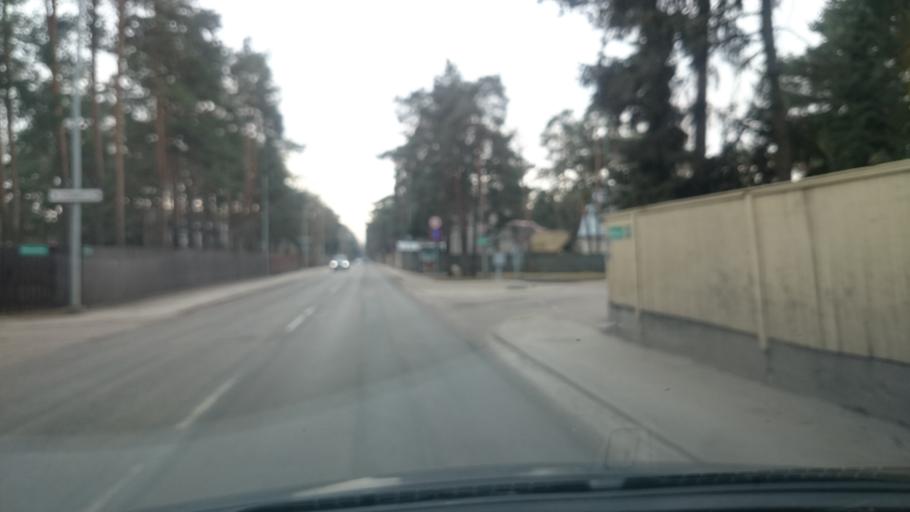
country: EE
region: Harju
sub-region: Saue vald
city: Laagri
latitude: 59.3794
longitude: 24.6366
